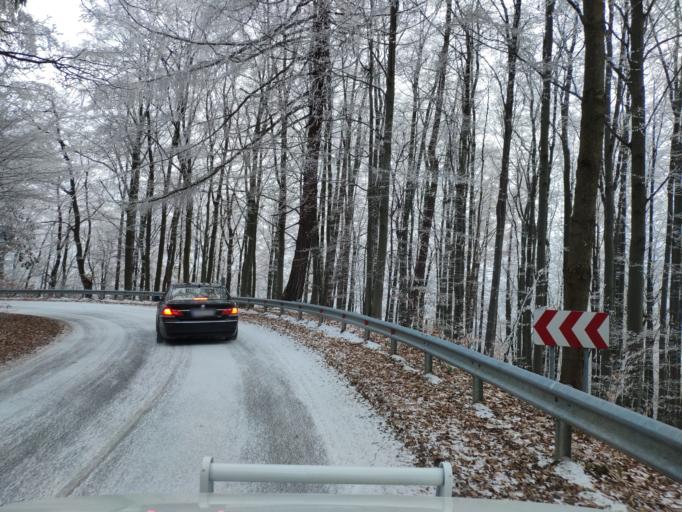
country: SK
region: Kosicky
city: Dobsina
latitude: 48.8007
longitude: 20.4940
